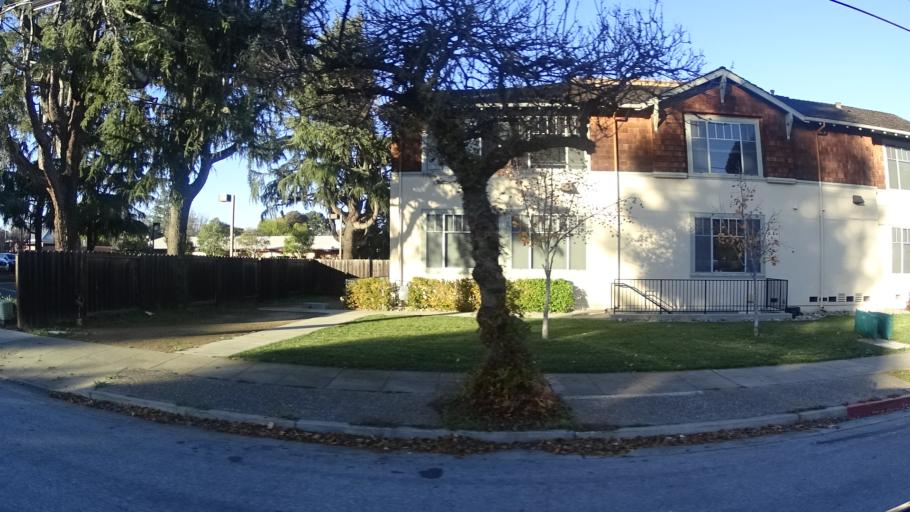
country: US
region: California
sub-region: Santa Clara County
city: Sunnyvale
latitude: 37.3677
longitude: -122.0265
